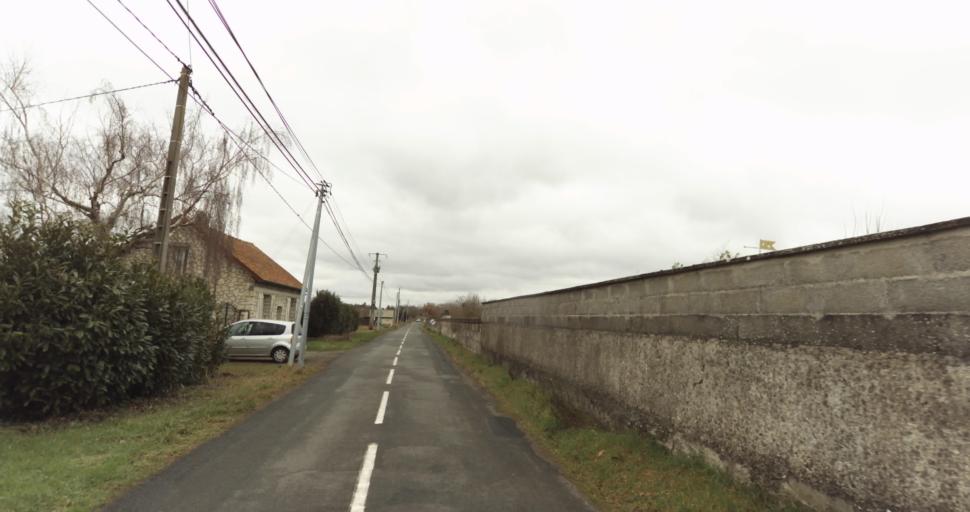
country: FR
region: Pays de la Loire
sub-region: Departement de Maine-et-Loire
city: Distre
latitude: 47.2422
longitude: -0.1058
